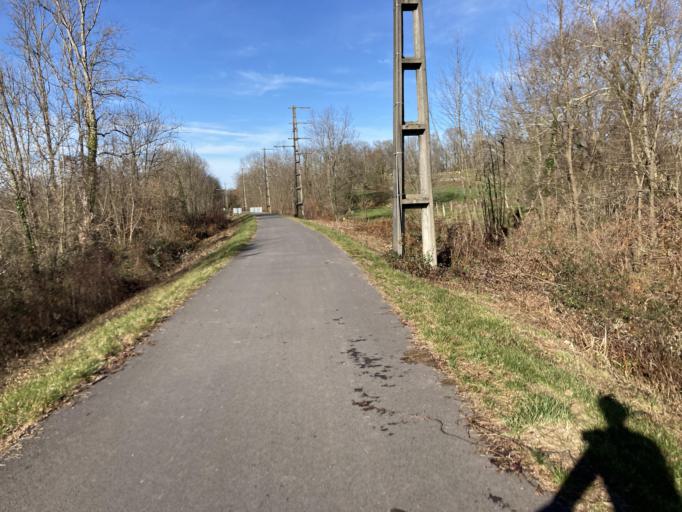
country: FR
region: Aquitaine
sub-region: Departement des Pyrenees-Atlantiques
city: Arudy
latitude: 43.1327
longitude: -0.4449
